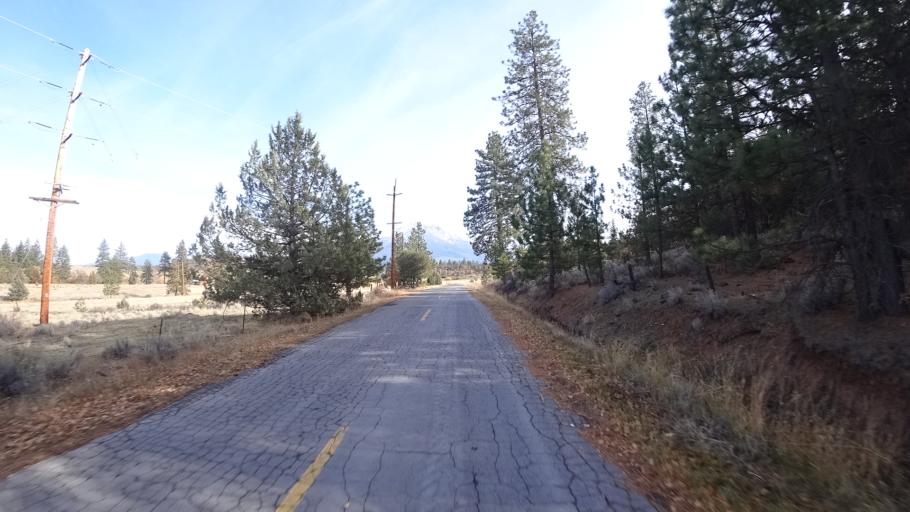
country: US
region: California
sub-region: Siskiyou County
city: Weed
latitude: 41.4660
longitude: -122.4047
